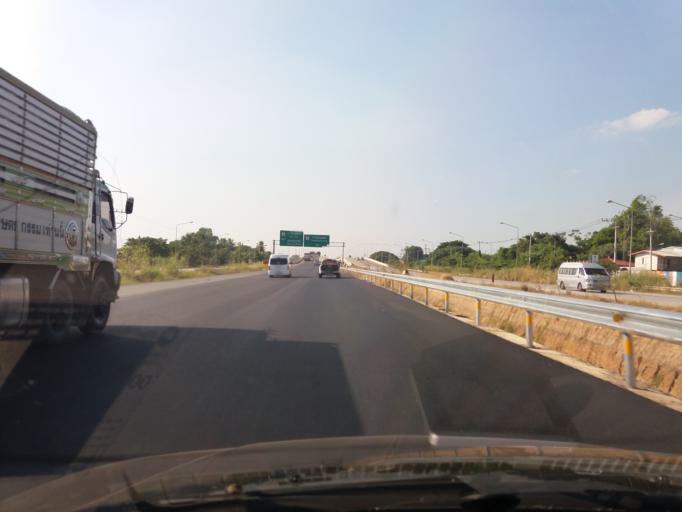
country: TH
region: Nakhon Sawan
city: Nakhon Sawan
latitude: 15.6302
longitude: 100.1047
